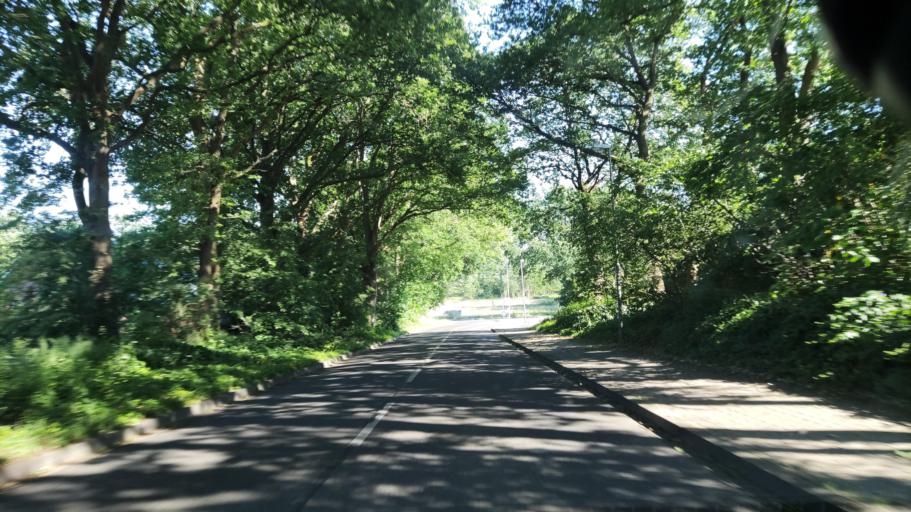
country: DE
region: Lower Saxony
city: Stelle
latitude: 53.3640
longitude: 10.1302
